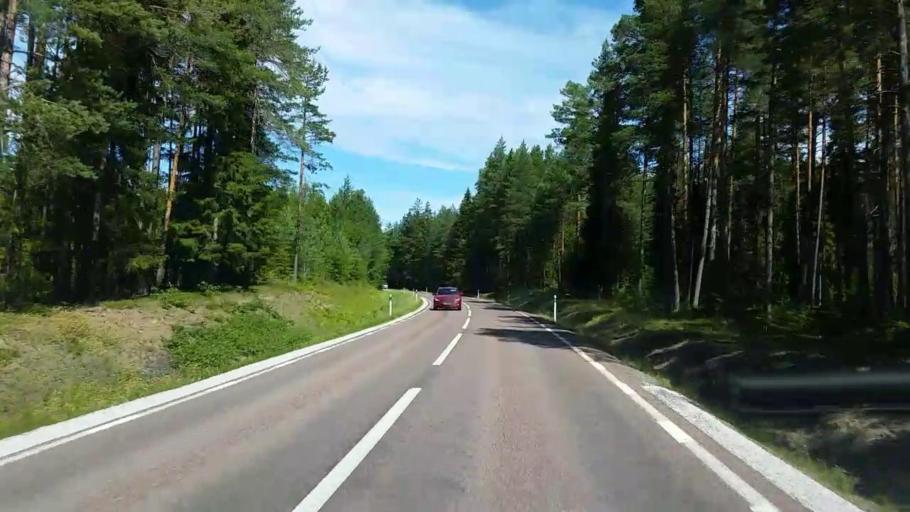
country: SE
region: Dalarna
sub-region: Rattviks Kommun
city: Raettvik
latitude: 60.9102
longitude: 15.1992
